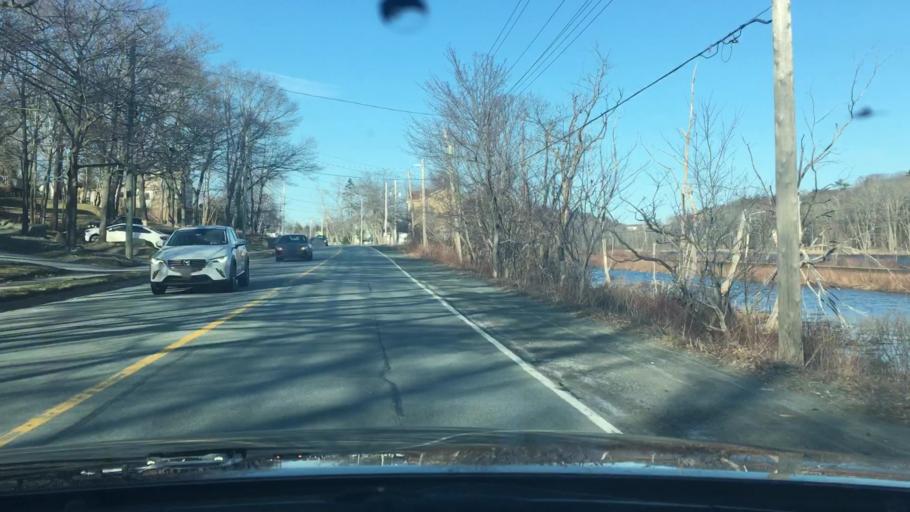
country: CA
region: Nova Scotia
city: Dartmouth
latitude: 44.7431
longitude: -63.6391
